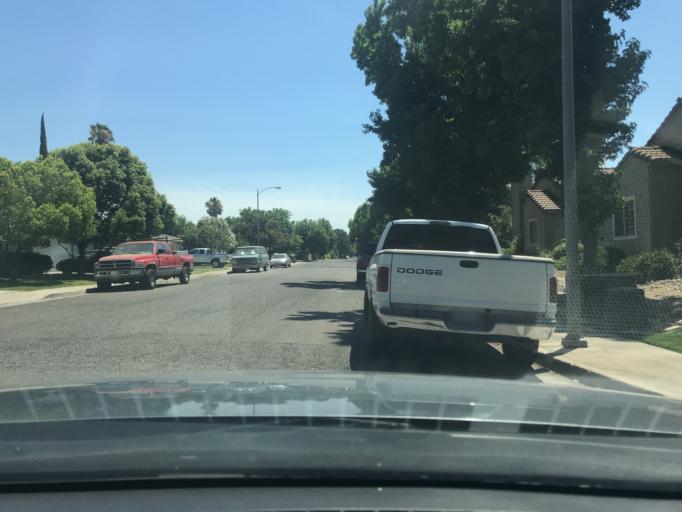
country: US
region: California
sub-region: Merced County
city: Merced
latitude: 37.3198
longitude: -120.5010
